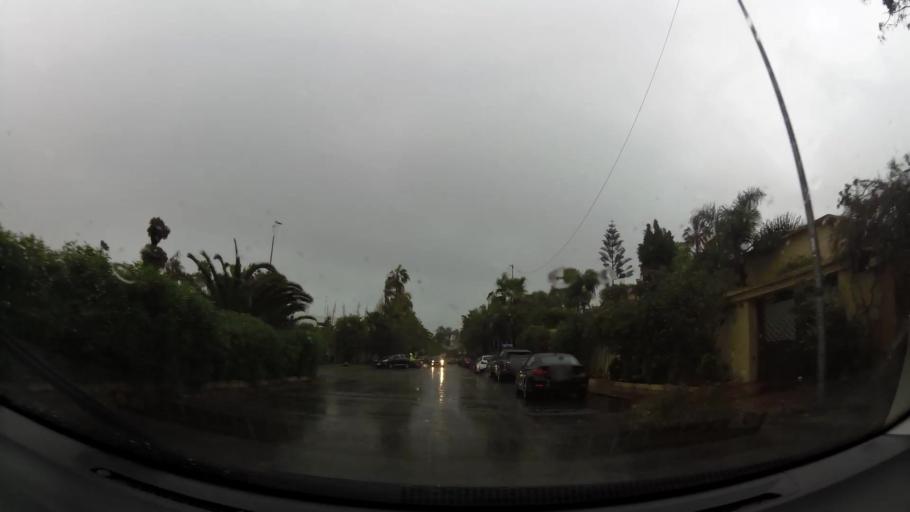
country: MA
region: Grand Casablanca
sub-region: Casablanca
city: Casablanca
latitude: 33.5911
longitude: -7.6690
